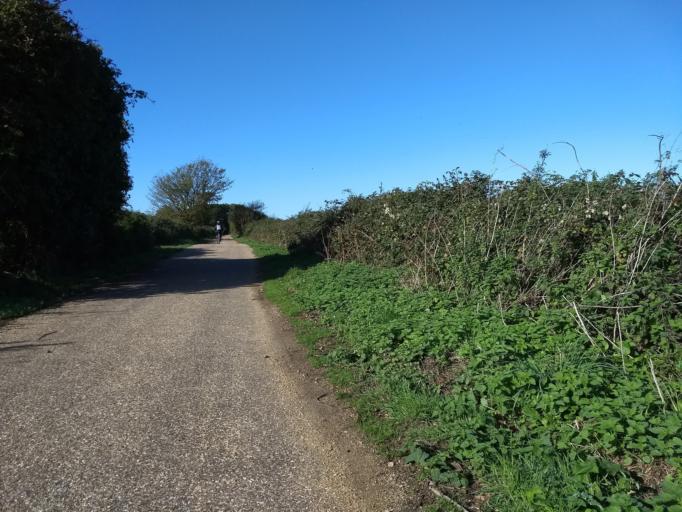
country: GB
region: England
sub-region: Isle of Wight
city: Shanklin
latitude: 50.6297
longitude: -1.2061
